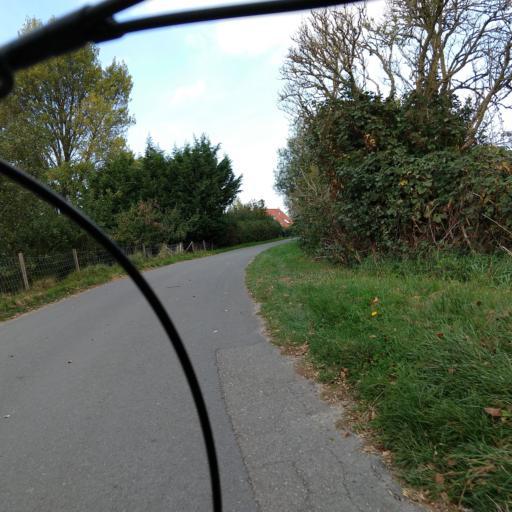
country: NL
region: South Holland
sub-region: Gemeente Goeree-Overflakkee
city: Ouddorp
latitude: 51.7159
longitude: 3.9470
